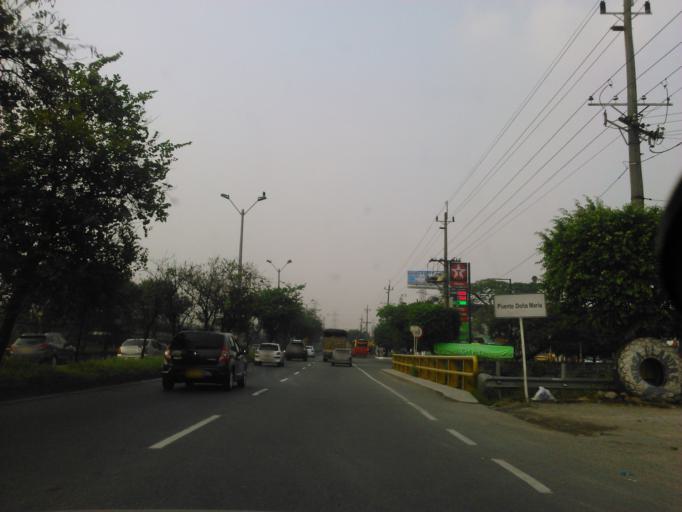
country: CO
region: Antioquia
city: Envigado
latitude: 6.1812
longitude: -75.5911
